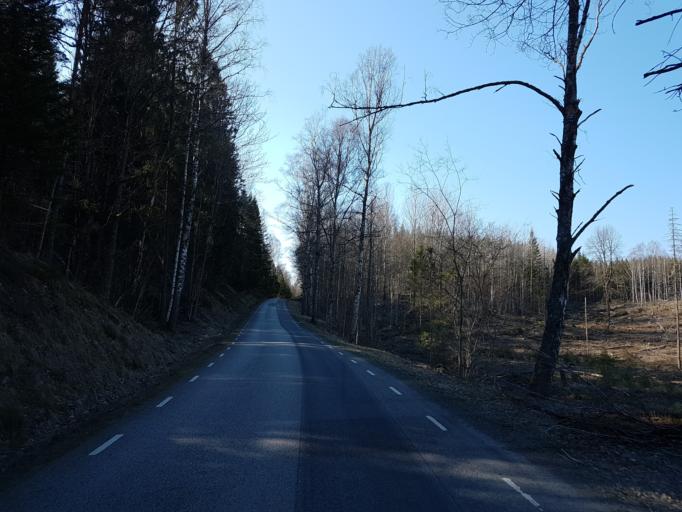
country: SE
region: Kalmar
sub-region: Vasterviks Kommun
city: Overum
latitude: 58.1689
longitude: 16.2618
